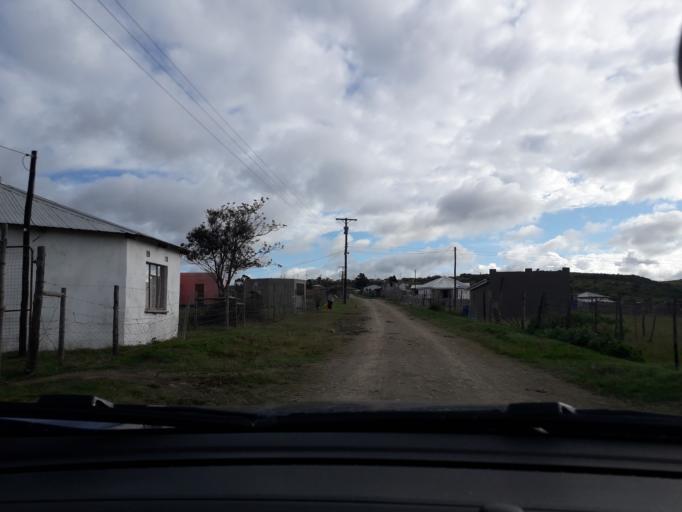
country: ZA
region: Eastern Cape
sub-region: Buffalo City Metropolitan Municipality
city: East London
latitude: -32.8040
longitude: 27.9640
